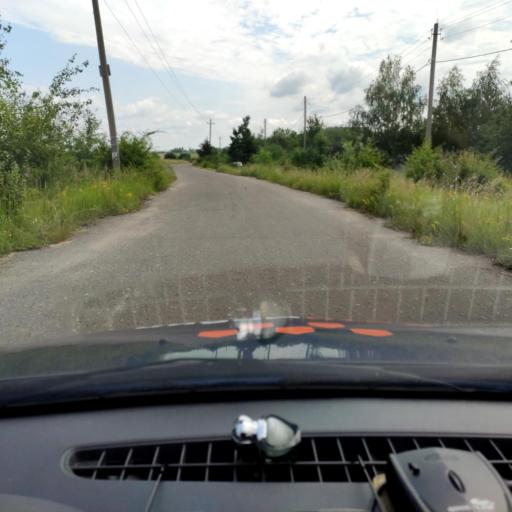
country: RU
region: Voronezj
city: Ramon'
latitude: 52.0760
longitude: 39.3119
